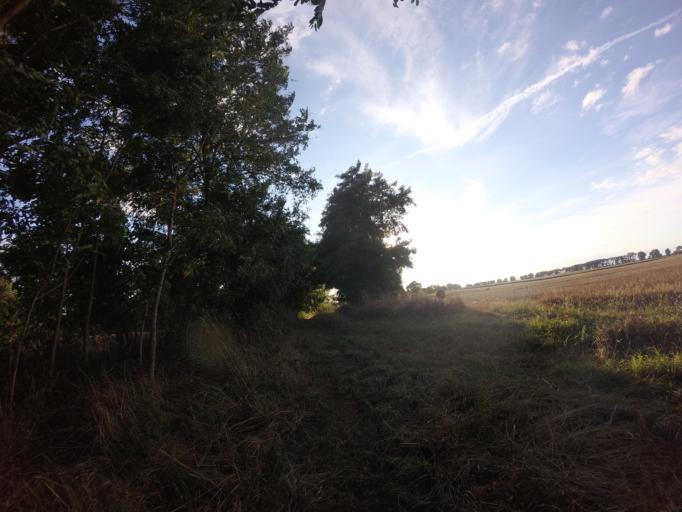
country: PL
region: West Pomeranian Voivodeship
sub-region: Powiat choszczenski
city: Choszczno
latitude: 53.1209
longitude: 15.4055
